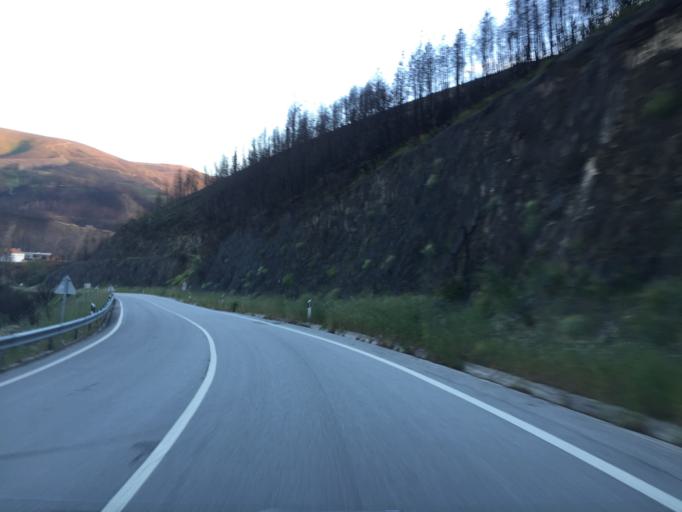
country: PT
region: Coimbra
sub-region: Pampilhosa da Serra
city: Pampilhosa da Serra
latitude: 40.0522
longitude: -7.9618
